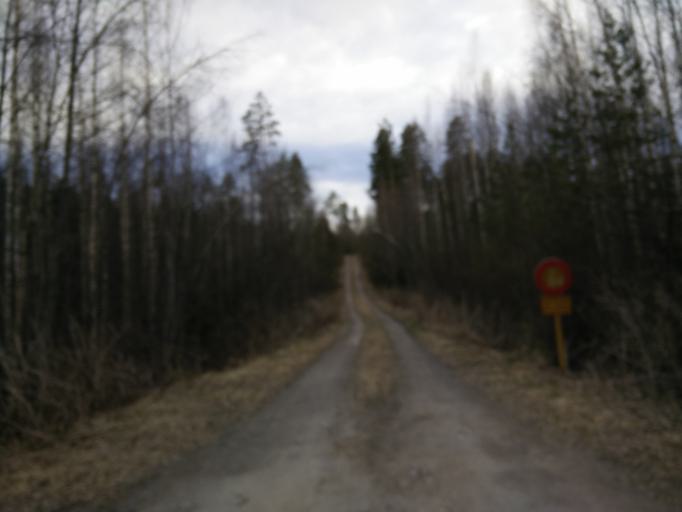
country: FI
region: Pirkanmaa
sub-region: Tampere
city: Orivesi
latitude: 61.6961
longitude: 24.3218
